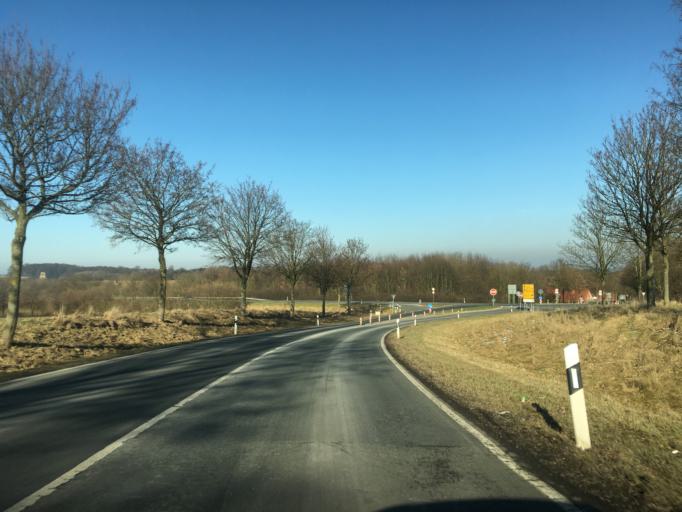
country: DE
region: North Rhine-Westphalia
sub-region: Regierungsbezirk Munster
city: Horstmar
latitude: 52.0769
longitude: 7.2938
